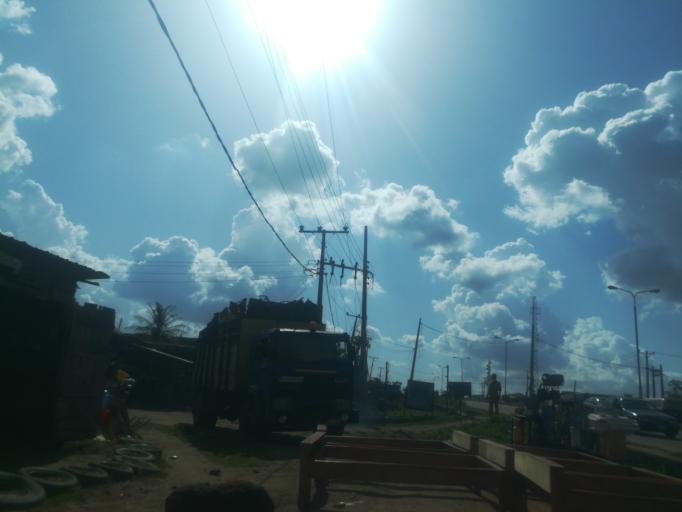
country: NG
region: Oyo
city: Egbeda
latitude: 7.4277
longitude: 3.9997
